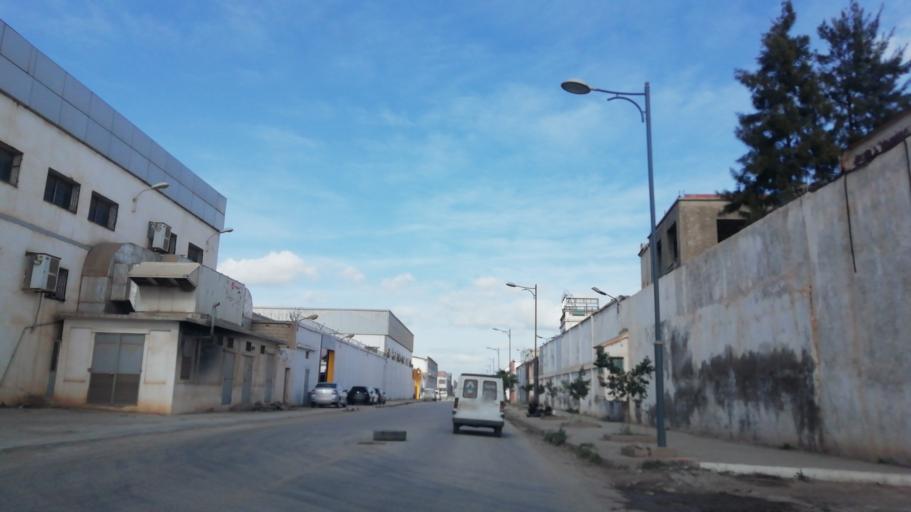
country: DZ
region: Oran
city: Es Senia
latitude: 35.6428
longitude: -0.5885
